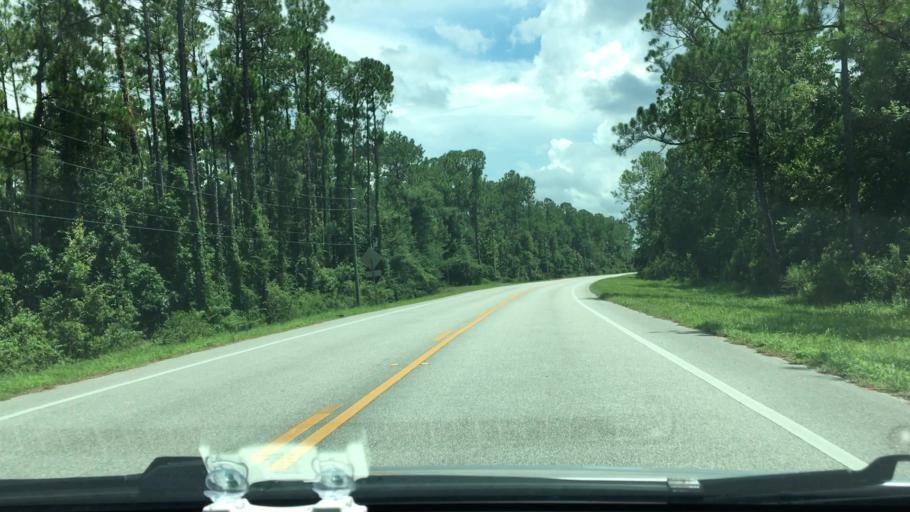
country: US
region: Florida
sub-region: Volusia County
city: Samsula-Spruce Creek
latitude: 29.0285
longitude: -81.0664
